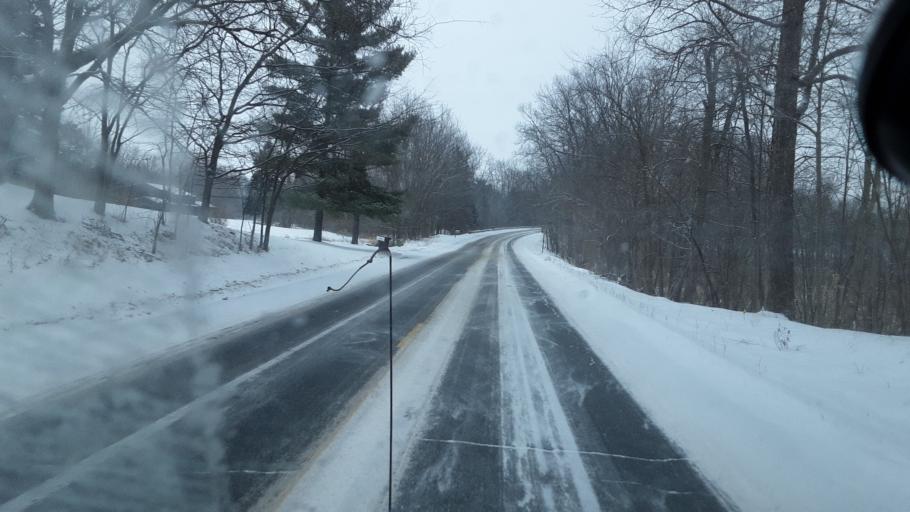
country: US
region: Michigan
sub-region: Ingham County
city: Mason
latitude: 42.5467
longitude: -84.3697
